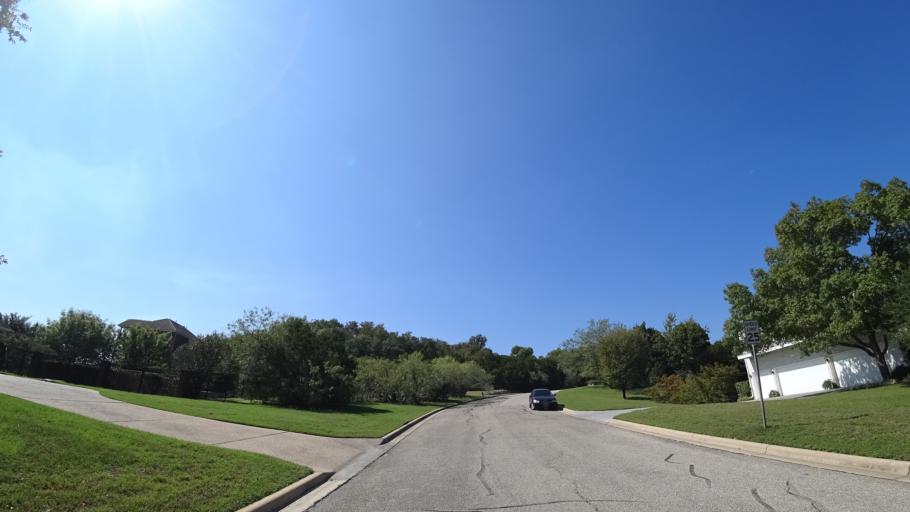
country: US
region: Texas
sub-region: Travis County
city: Rollingwood
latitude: 30.2794
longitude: -97.7962
